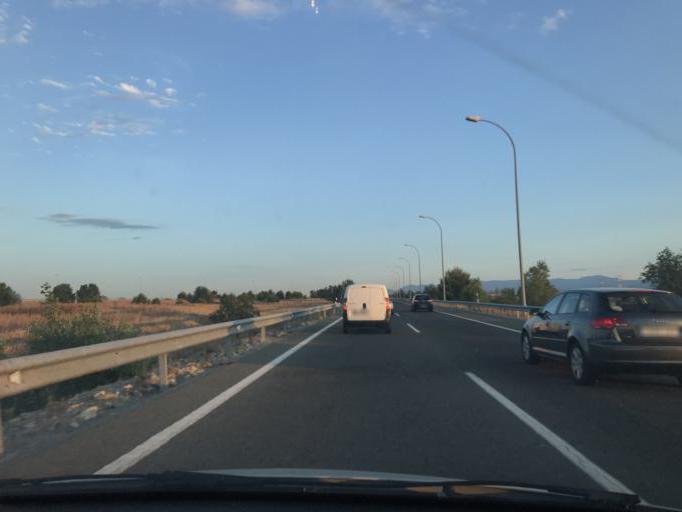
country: ES
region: Madrid
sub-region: Provincia de Madrid
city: San Sebastian de los Reyes
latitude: 40.5450
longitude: -3.5684
